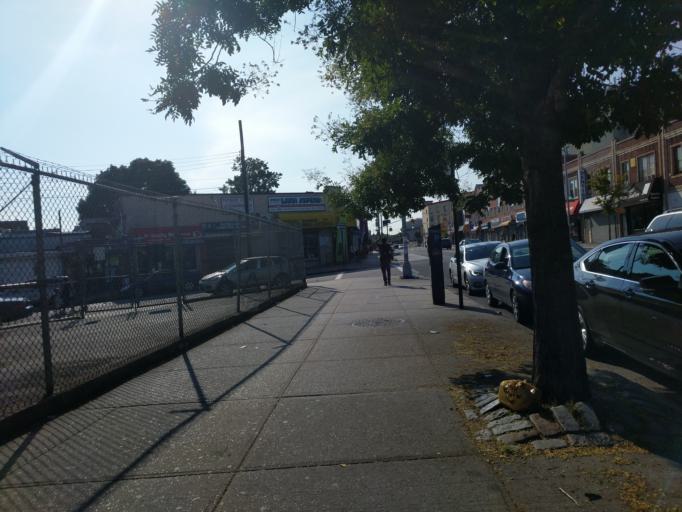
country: US
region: New York
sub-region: Queens County
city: Jamaica
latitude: 40.7020
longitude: -73.8104
